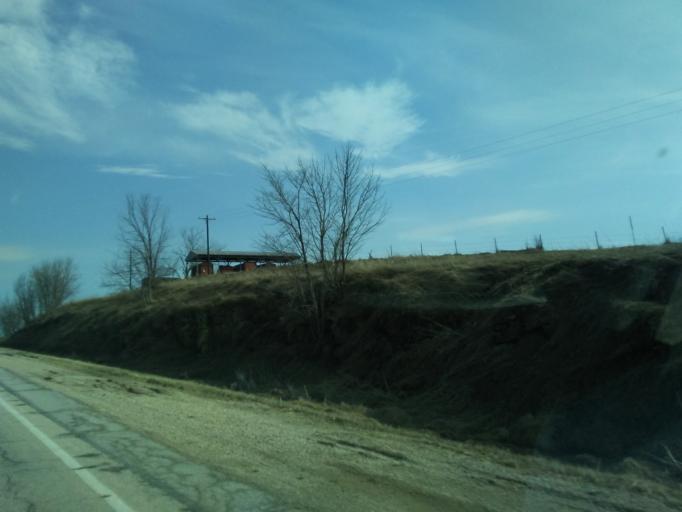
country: US
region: Wisconsin
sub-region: Crawford County
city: Prairie du Chien
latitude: 43.1322
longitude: -91.2236
